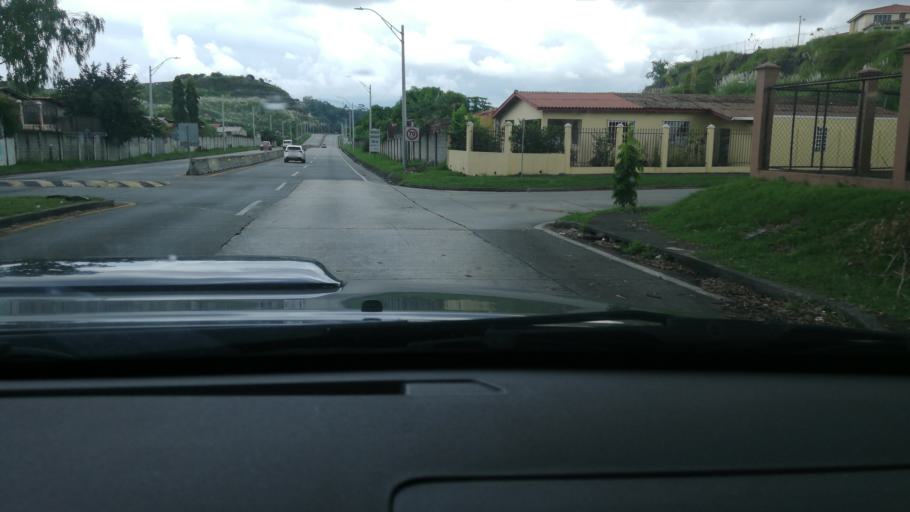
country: PA
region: Panama
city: San Miguelito
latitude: 9.0530
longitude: -79.4839
